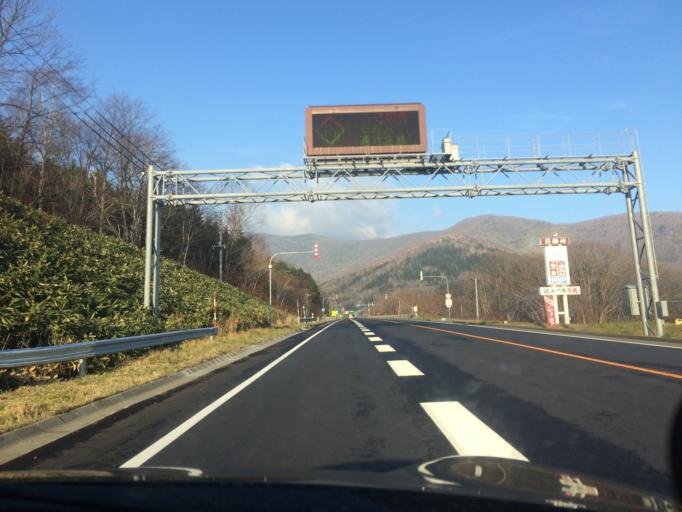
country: JP
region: Hokkaido
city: Otofuke
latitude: 42.9738
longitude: 142.8058
